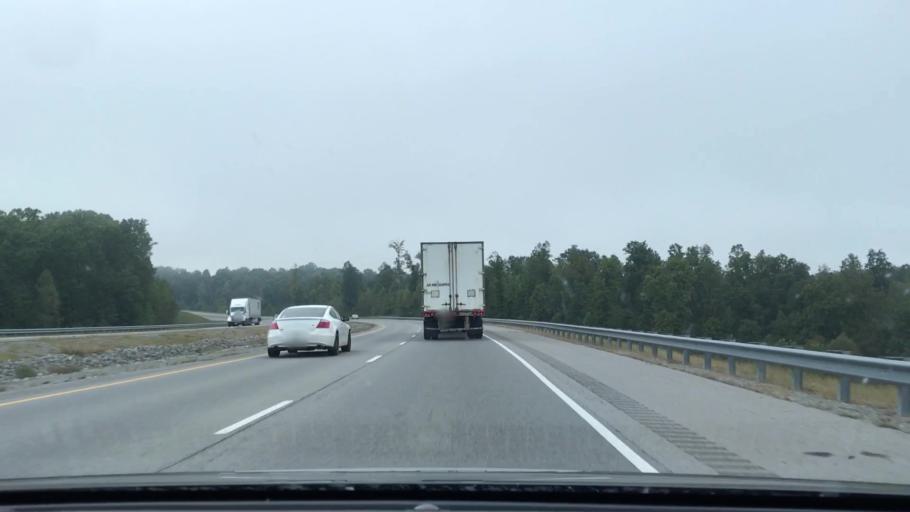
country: US
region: Tennessee
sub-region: Sumner County
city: Gallatin
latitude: 36.4831
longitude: -86.4803
